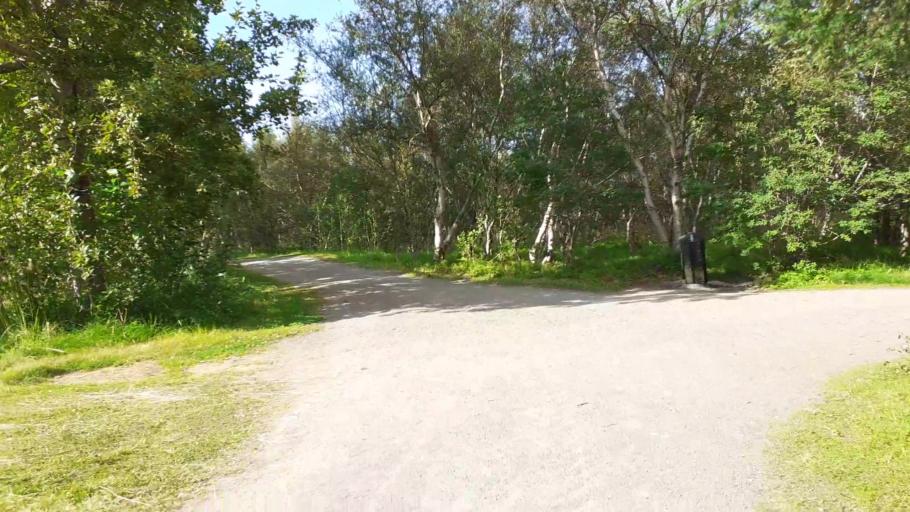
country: IS
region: Northeast
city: Akureyri
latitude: 65.6455
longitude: -18.0854
